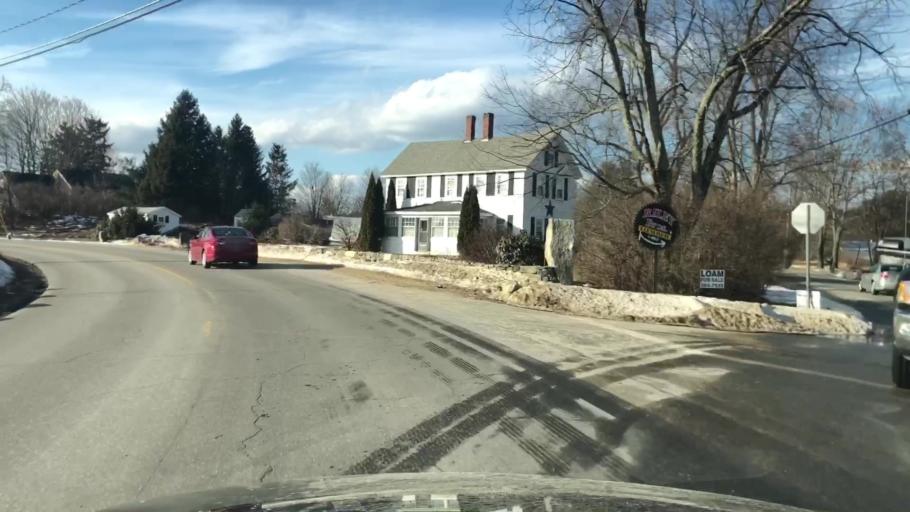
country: US
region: New Hampshire
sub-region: Hillsborough County
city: Milford
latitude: 42.8482
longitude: -71.6710
